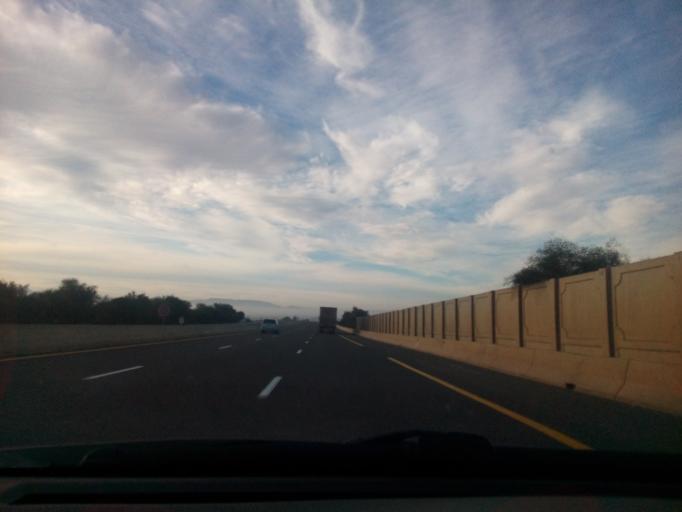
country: DZ
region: Relizane
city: Relizane
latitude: 35.7265
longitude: 0.3019
